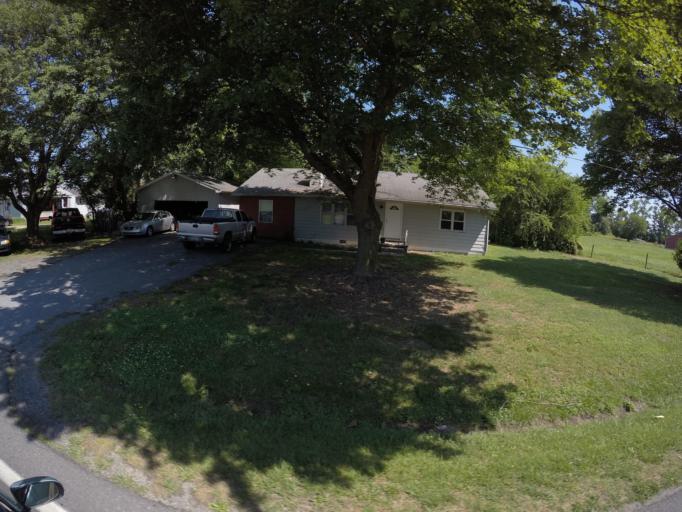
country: US
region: Delaware
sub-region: Sussex County
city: Georgetown
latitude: 38.6822
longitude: -75.3534
